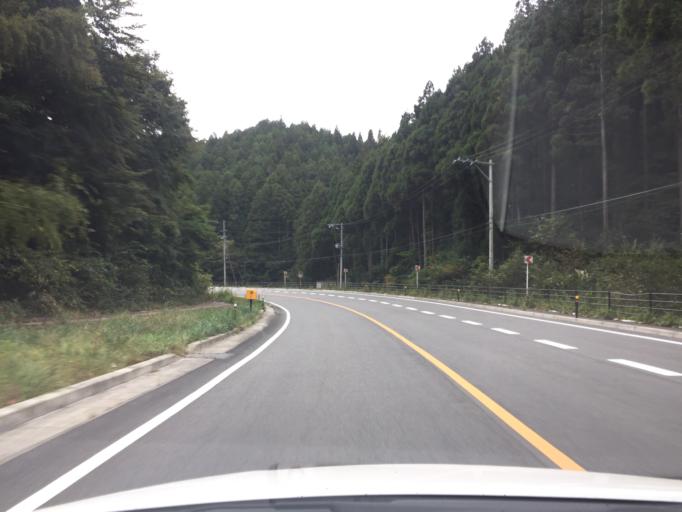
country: JP
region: Ibaraki
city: Kitaibaraki
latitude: 36.9069
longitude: 140.7218
